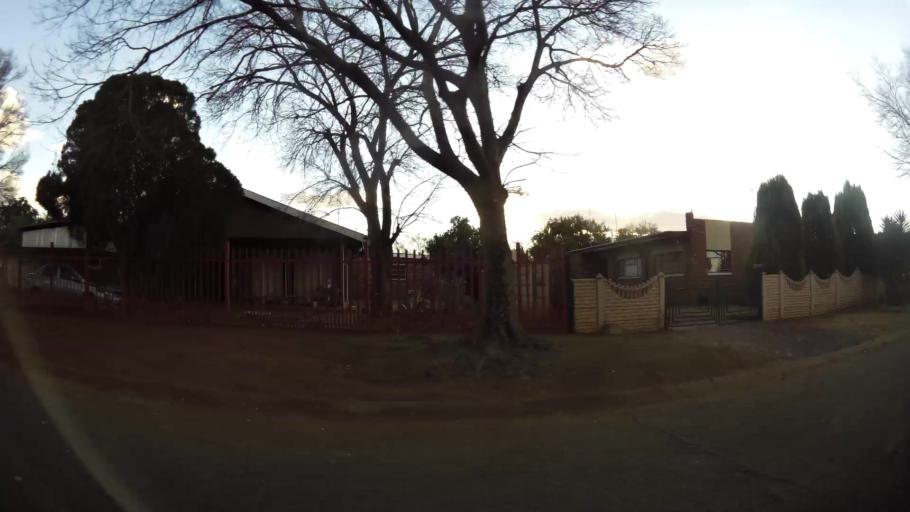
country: ZA
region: North-West
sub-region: Dr Kenneth Kaunda District Municipality
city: Potchefstroom
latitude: -26.7393
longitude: 27.0933
